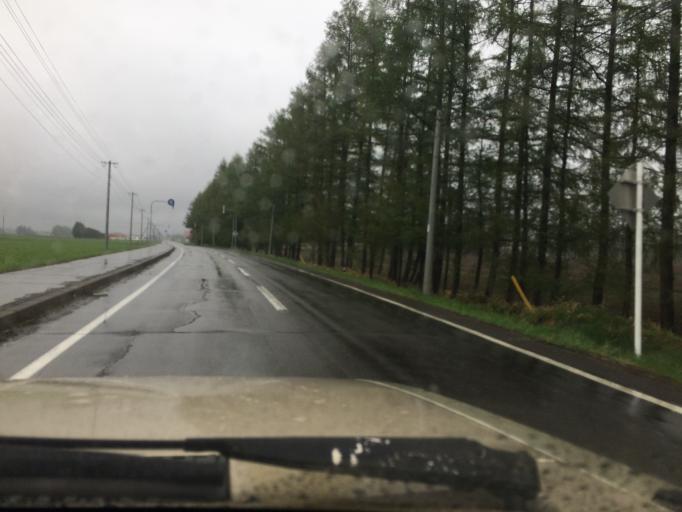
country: JP
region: Hokkaido
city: Obihiro
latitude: 42.8480
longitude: 143.0020
